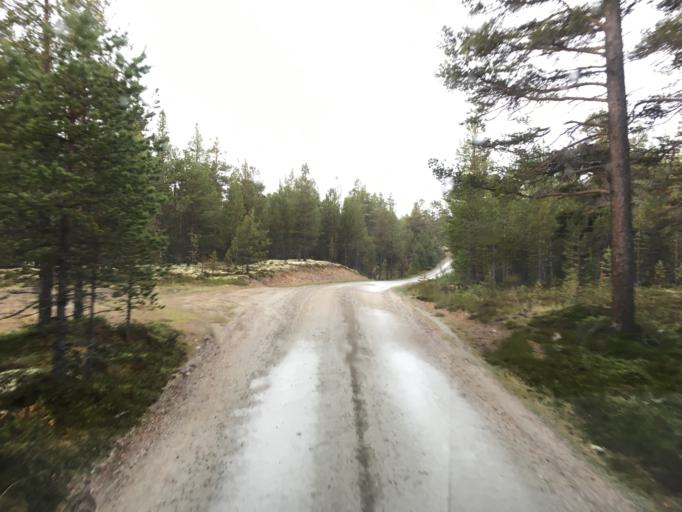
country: NO
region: Hedmark
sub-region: Folldal
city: Folldal
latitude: 62.0697
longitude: 9.9390
